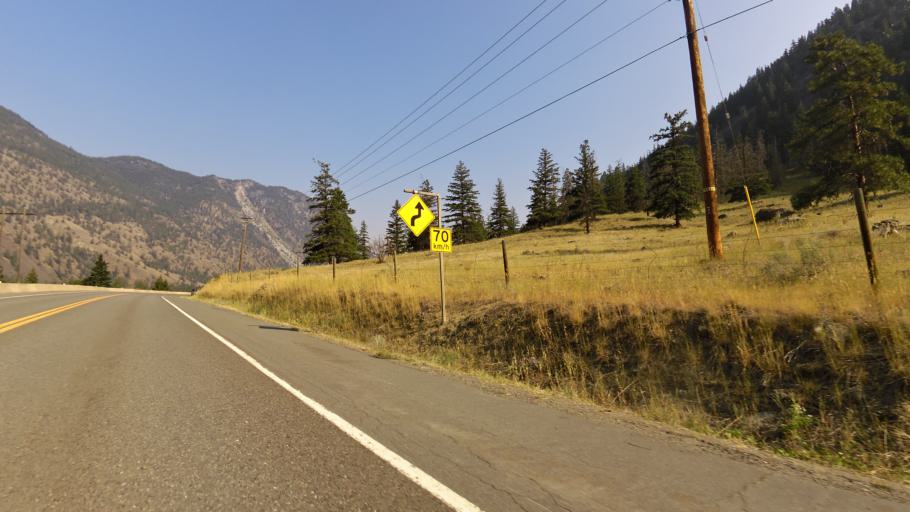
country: CA
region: British Columbia
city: Summerland
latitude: 49.2771
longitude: -120.0244
